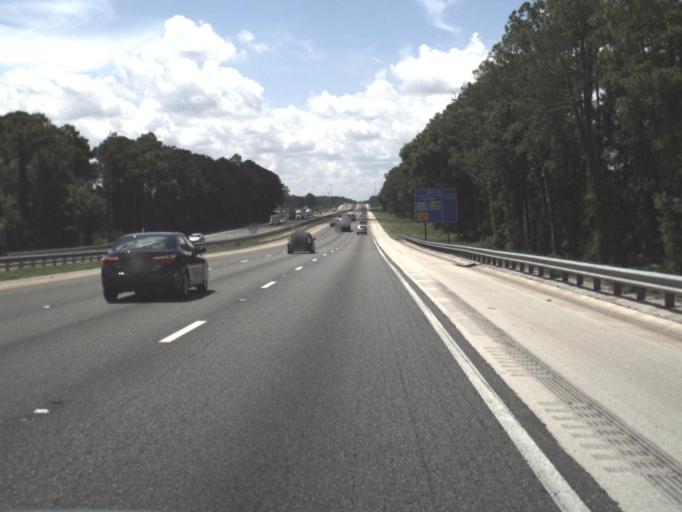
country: US
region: Florida
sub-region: Saint Johns County
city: Saint Augustine South
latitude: 29.8389
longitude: -81.3859
